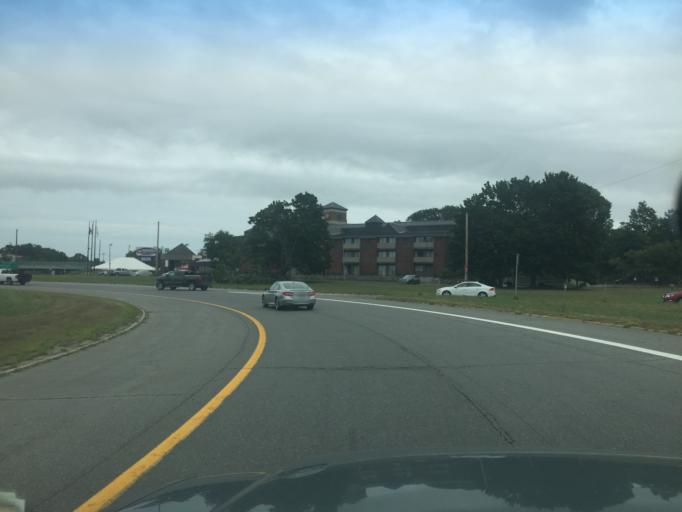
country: US
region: New Hampshire
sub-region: Rockingham County
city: Portsmouth
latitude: 43.0723
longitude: -70.7806
